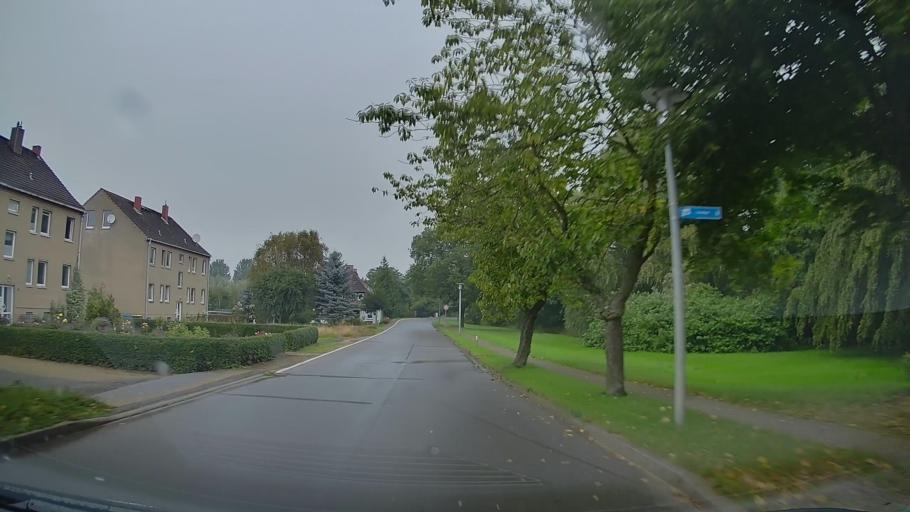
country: DE
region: Mecklenburg-Vorpommern
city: Kalkhorst
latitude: 53.9977
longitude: 11.0437
